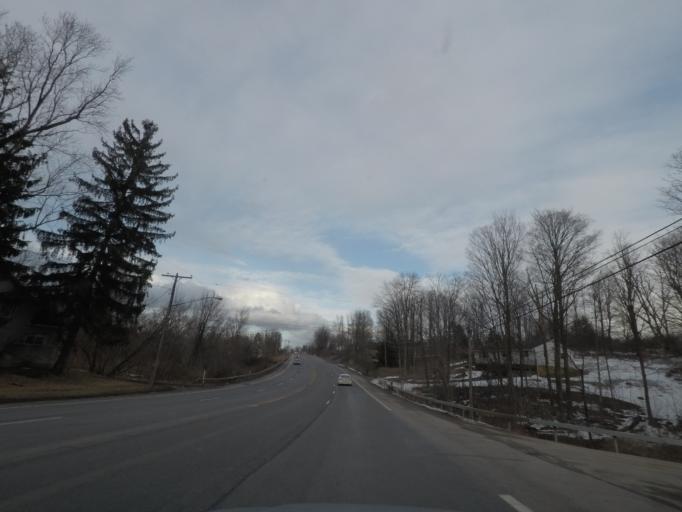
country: US
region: New York
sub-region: Oneida County
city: Clark Mills
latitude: 43.0762
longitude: -75.4391
